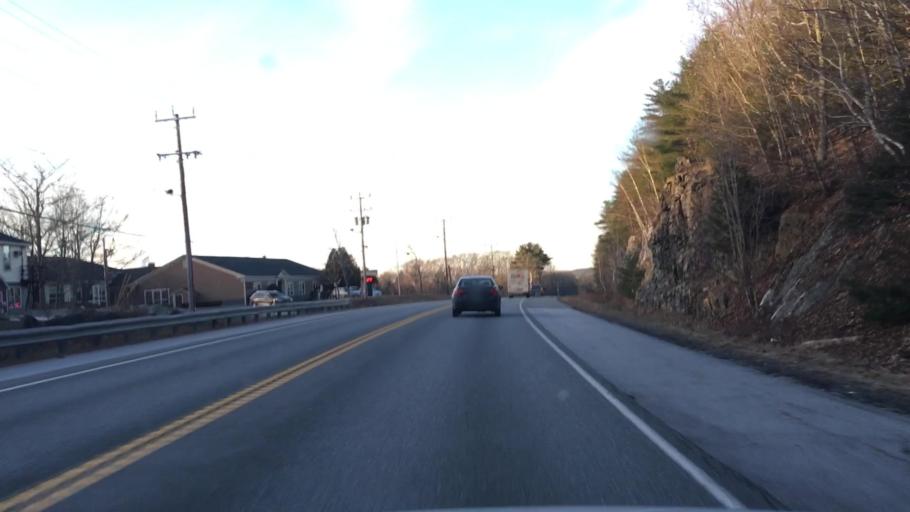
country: US
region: Maine
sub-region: Hancock County
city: Dedham
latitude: 44.7264
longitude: -68.6217
